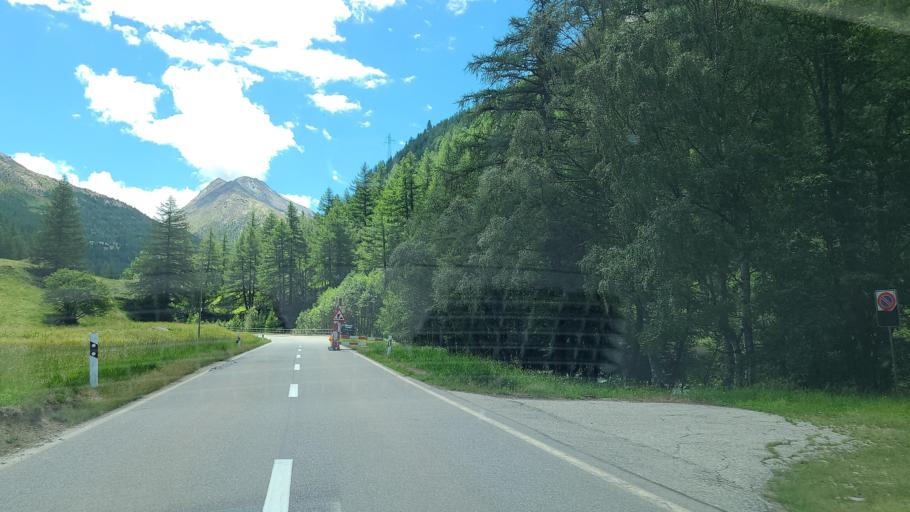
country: CH
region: Valais
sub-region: Visp District
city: Saas-Fee
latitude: 46.1041
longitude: 7.9479
